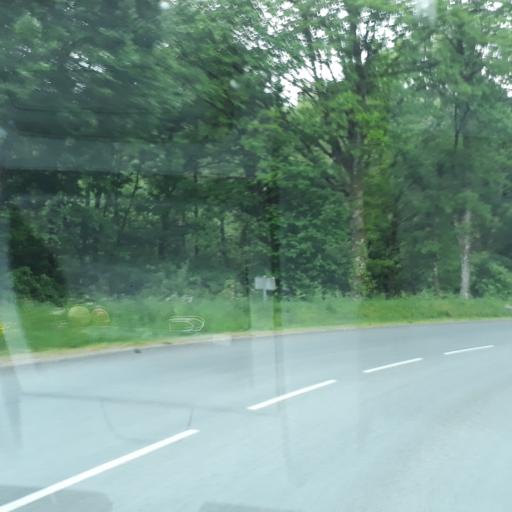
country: FR
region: Limousin
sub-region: Departement de la Haute-Vienne
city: Eymoutiers
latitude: 45.7630
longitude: 1.7498
